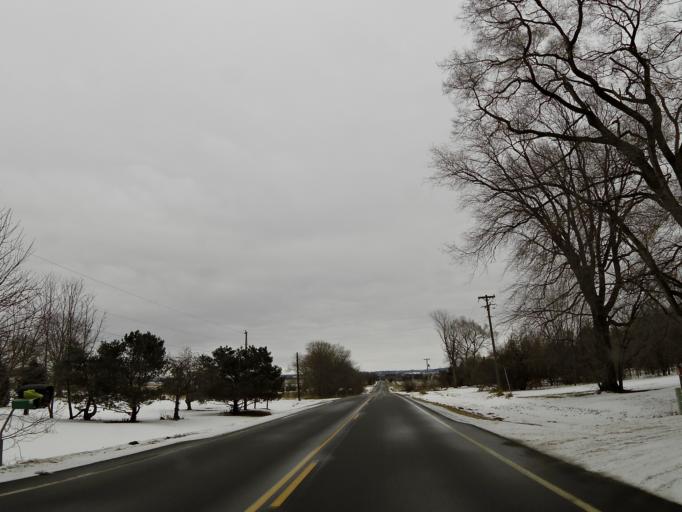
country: US
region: Minnesota
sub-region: Dakota County
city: Hastings
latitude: 44.7901
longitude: -92.8483
